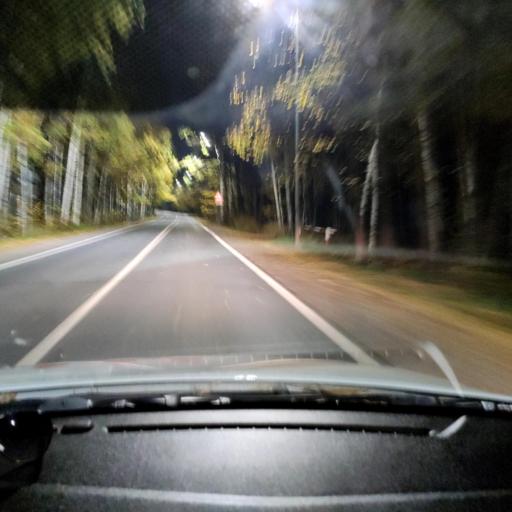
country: RU
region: Tatarstan
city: Verkhniy Uslon
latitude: 55.6297
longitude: 49.0151
